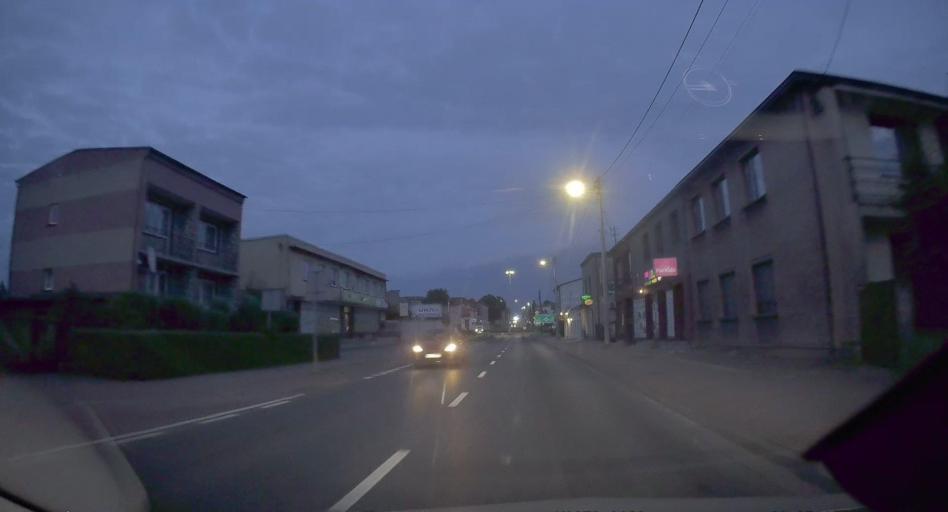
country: PL
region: Silesian Voivodeship
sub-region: Powiat klobucki
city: Klobuck
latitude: 50.9014
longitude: 18.9348
